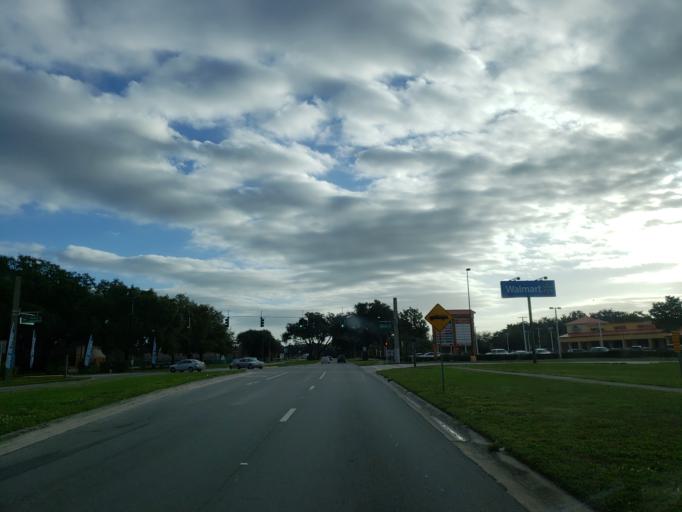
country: US
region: Florida
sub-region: Hillsborough County
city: Plant City
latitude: 27.9890
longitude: -82.1194
